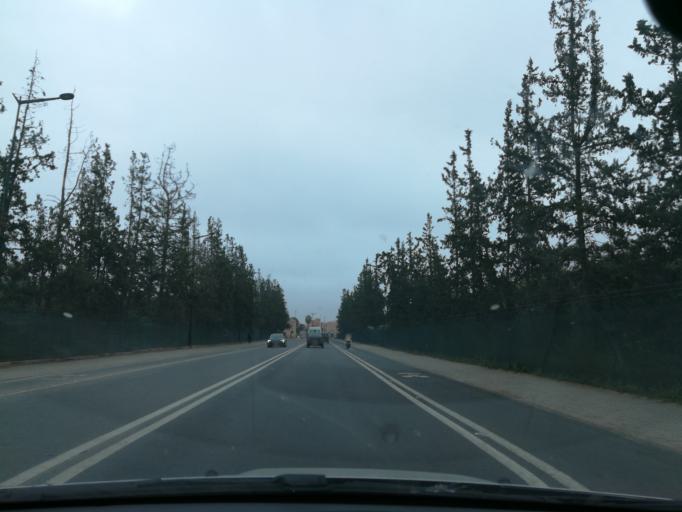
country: MA
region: Marrakech-Tensift-Al Haouz
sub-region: Marrakech
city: Marrakesh
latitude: 31.6033
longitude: -7.9747
